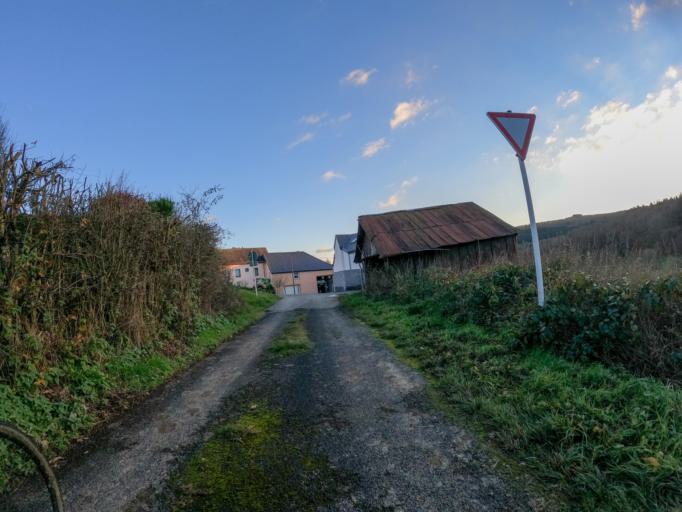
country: LU
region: Diekirch
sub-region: Canton de Wiltz
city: Bavigne
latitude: 49.9257
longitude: 5.8463
